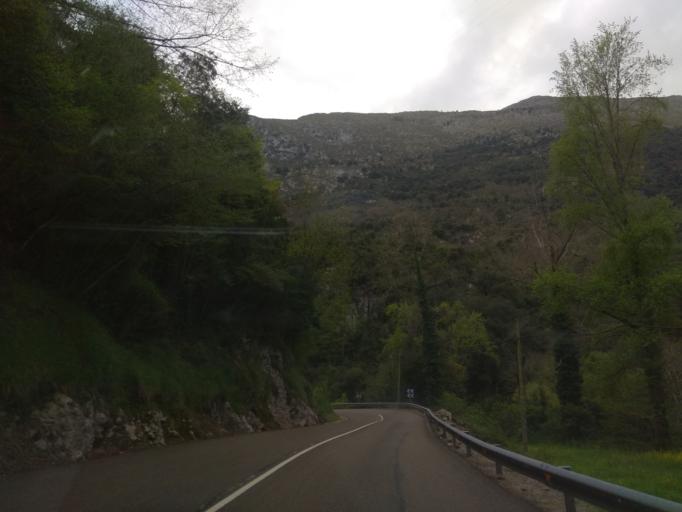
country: ES
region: Cantabria
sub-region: Provincia de Cantabria
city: Tresviso
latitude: 43.3109
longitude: -4.6088
